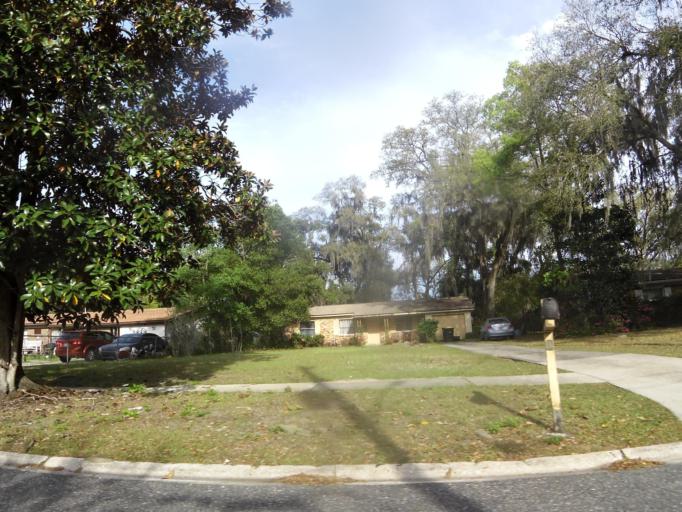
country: US
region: Florida
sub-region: Clay County
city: Bellair-Meadowbrook Terrace
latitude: 30.2449
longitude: -81.7695
